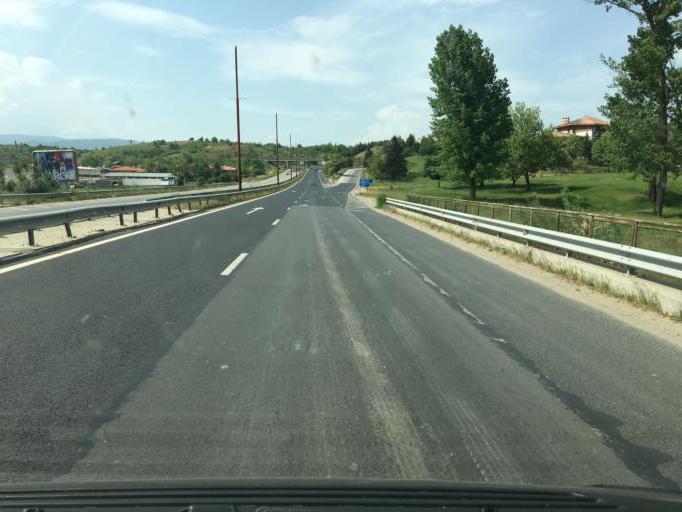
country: BG
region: Blagoevgrad
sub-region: Obshtina Blagoevgrad
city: Blagoevgrad
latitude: 42.0307
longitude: 23.0561
